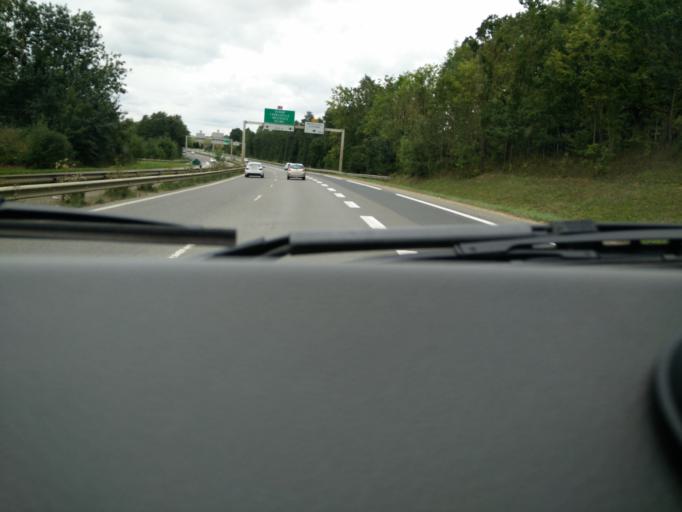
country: FR
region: Champagne-Ardenne
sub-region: Departement des Ardennes
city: Bazeilles
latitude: 49.6849
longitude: 4.9884
